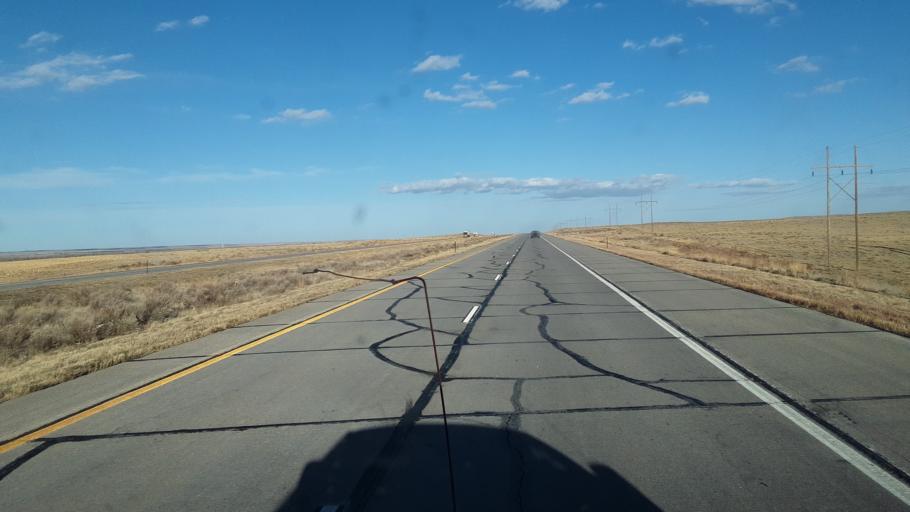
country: US
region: Nebraska
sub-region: Cheyenne County
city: Sidney
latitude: 40.8061
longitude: -102.8541
